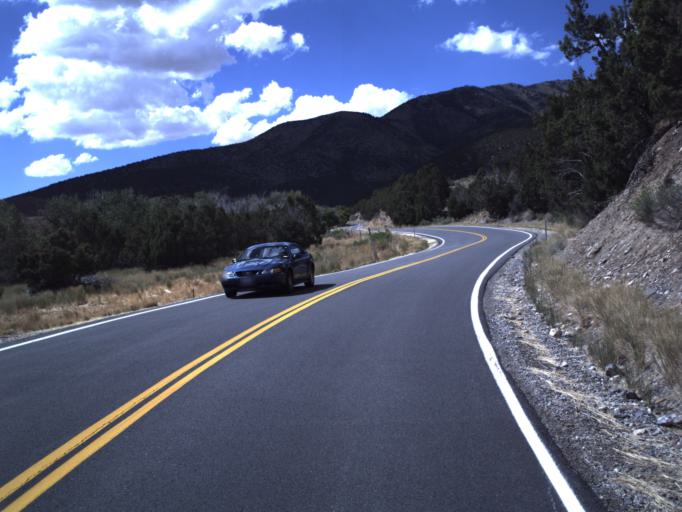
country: US
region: Utah
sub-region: Tooele County
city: Grantsville
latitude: 40.3421
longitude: -112.5415
